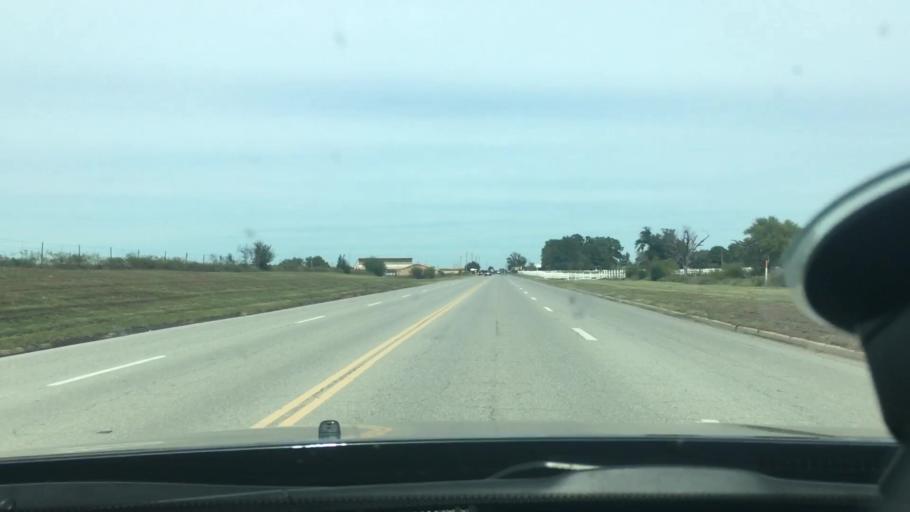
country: US
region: Oklahoma
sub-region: Atoka County
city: Atoka
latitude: 34.3882
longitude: -96.1455
